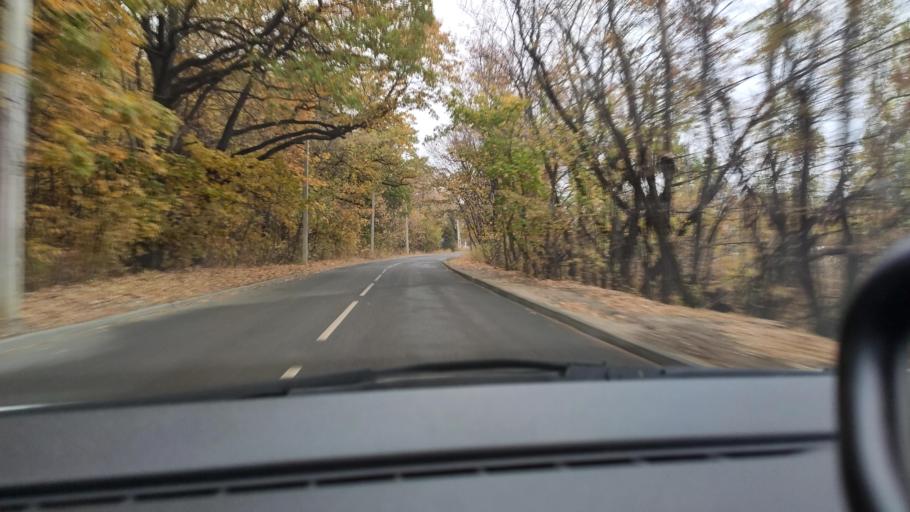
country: RU
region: Voronezj
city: Voronezh
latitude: 51.7242
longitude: 39.2355
